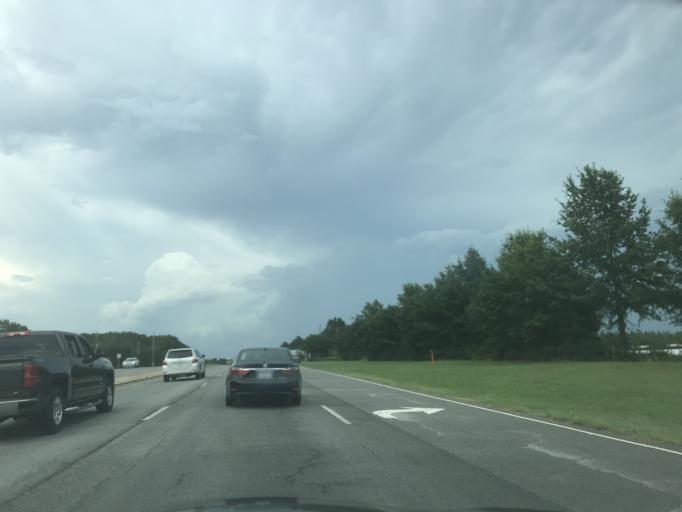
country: US
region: North Carolina
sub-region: Johnston County
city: Clayton
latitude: 35.6647
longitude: -78.4959
